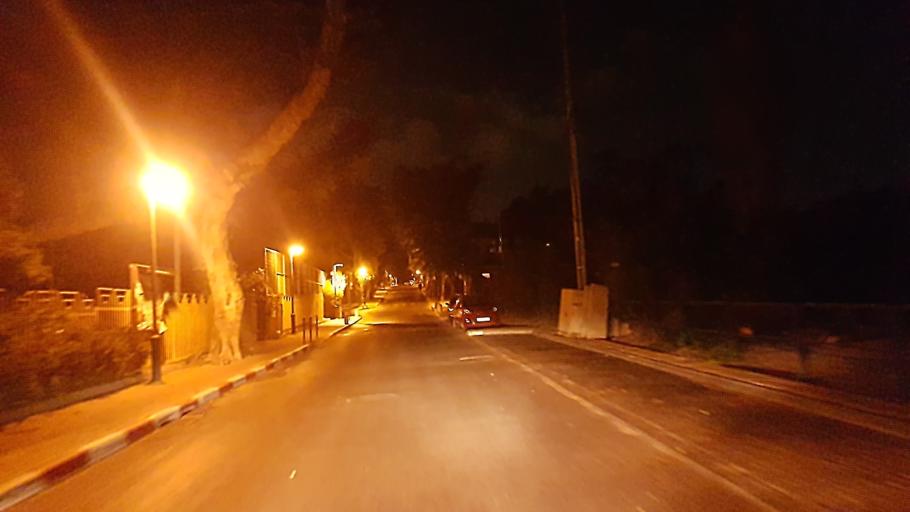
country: IL
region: Central District
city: Hod HaSharon
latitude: 32.1651
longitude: 34.8866
